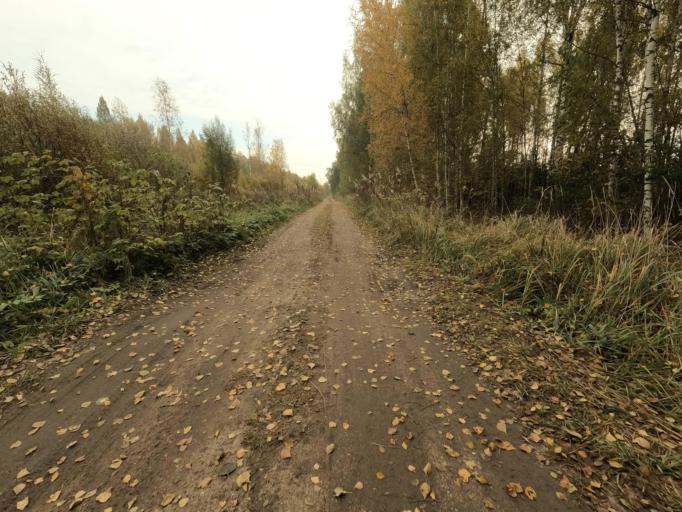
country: RU
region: Novgorod
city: Pankovka
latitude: 58.8708
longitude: 30.8974
